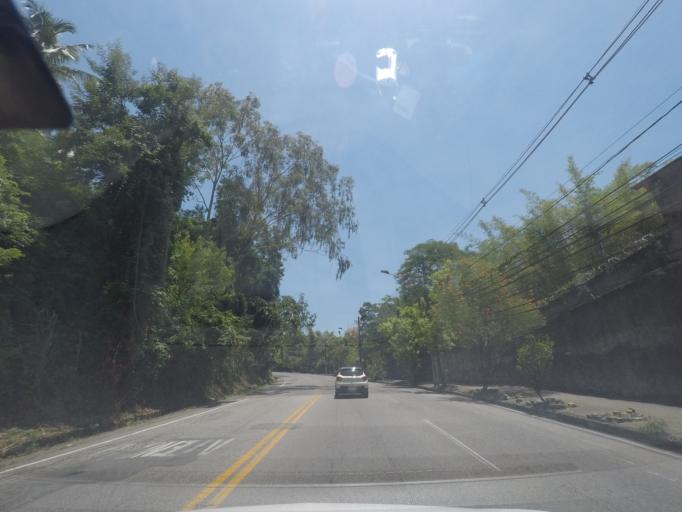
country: BR
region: Rio de Janeiro
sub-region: Niteroi
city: Niteroi
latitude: -22.9161
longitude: -43.0645
